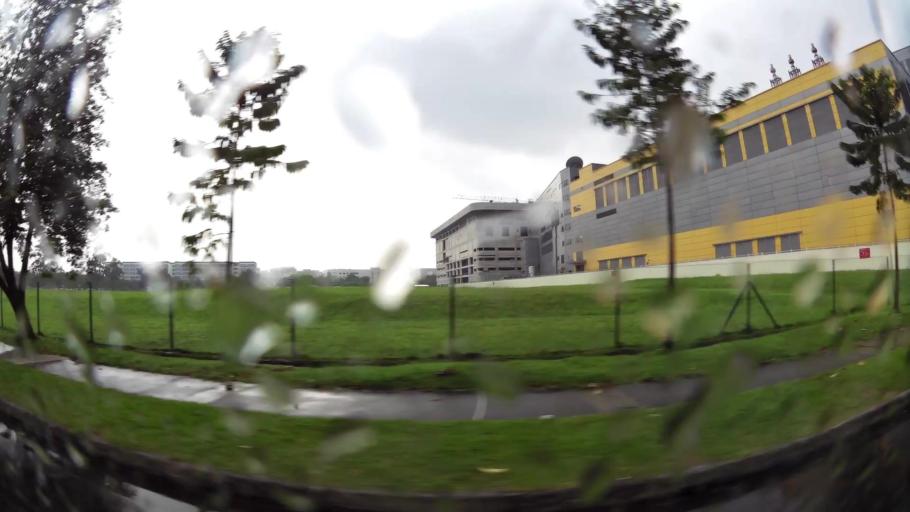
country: MY
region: Johor
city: Kampung Pasir Gudang Baru
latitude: 1.3894
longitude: 103.8487
